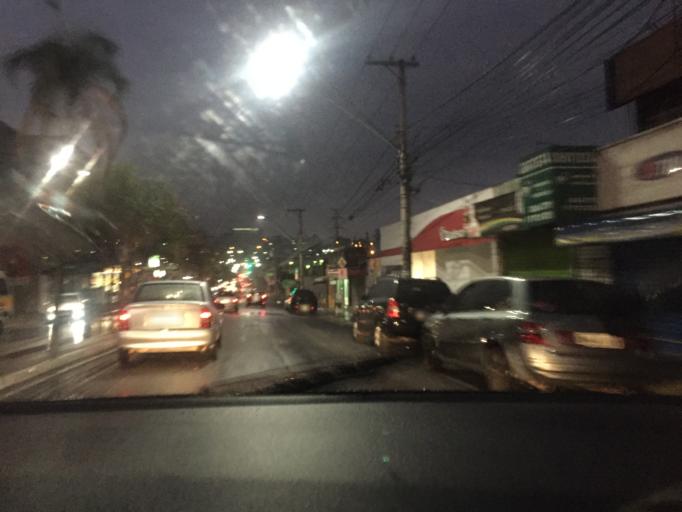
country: BR
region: Sao Paulo
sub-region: Varzea Paulista
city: Varzea Paulista
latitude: -23.2129
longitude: -46.8378
